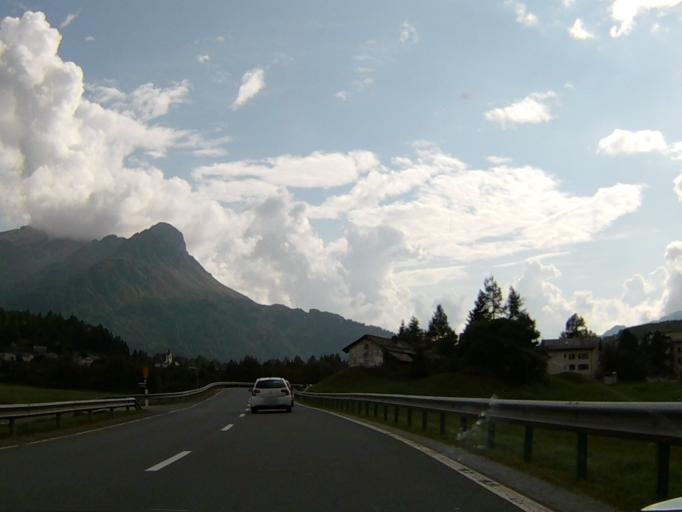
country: CH
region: Grisons
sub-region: Maloja District
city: Silvaplana
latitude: 46.4097
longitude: 9.7043
